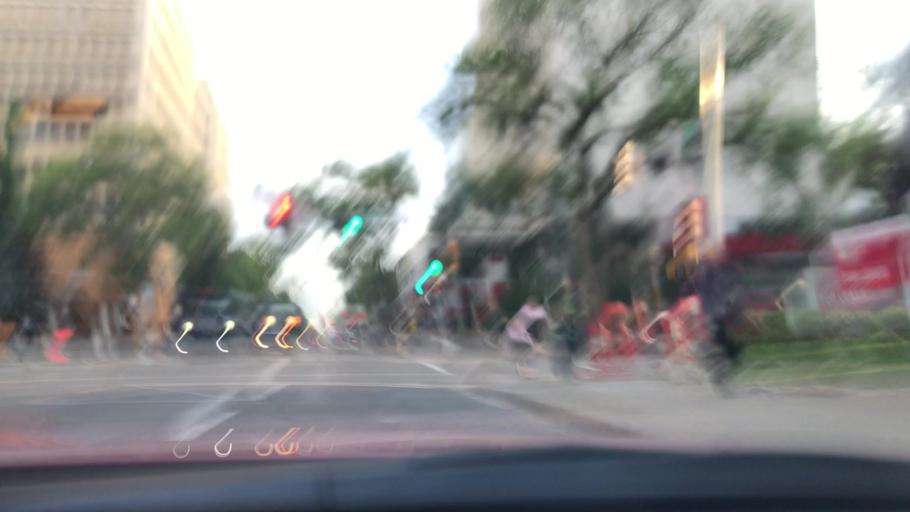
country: CA
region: Alberta
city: Edmonton
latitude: 53.5385
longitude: -113.5048
